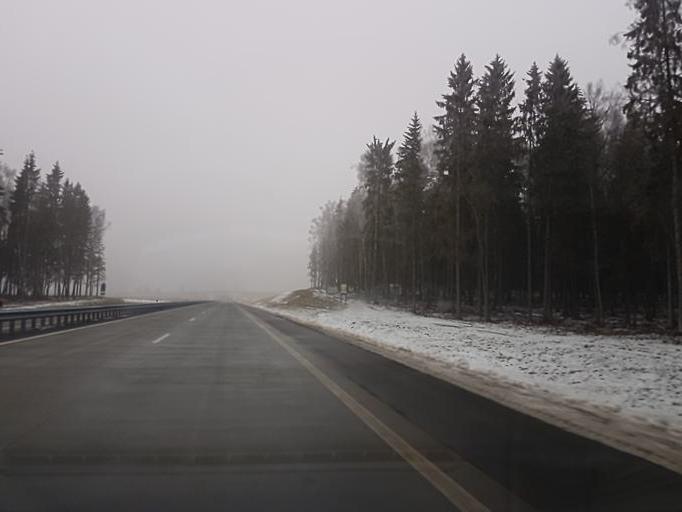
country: BY
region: Minsk
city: Atolina
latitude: 53.7245
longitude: 27.4279
